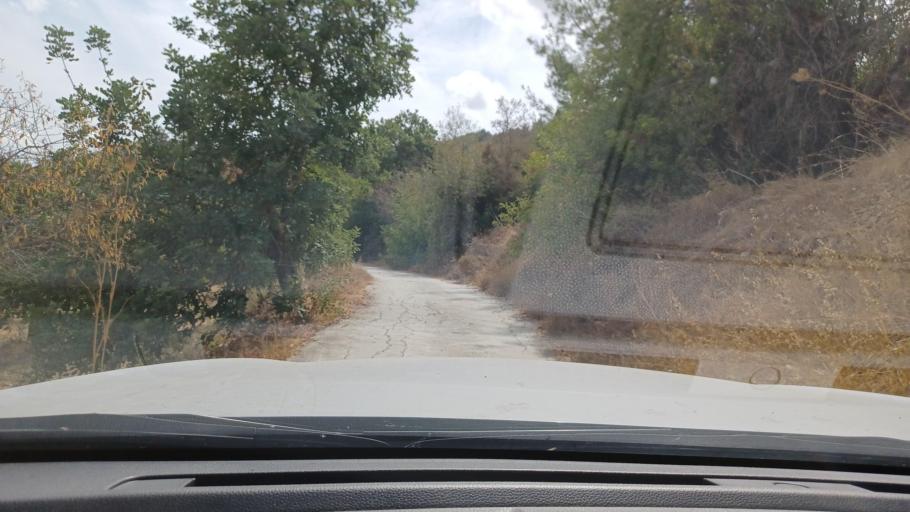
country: CY
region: Pafos
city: Polis
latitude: 35.0011
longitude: 32.5254
